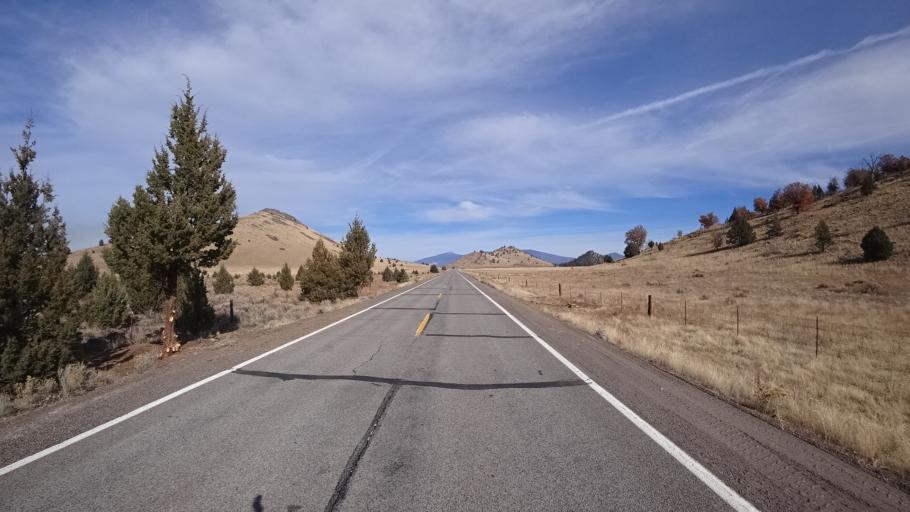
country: US
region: California
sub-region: Siskiyou County
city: Weed
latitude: 41.4880
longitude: -122.4072
